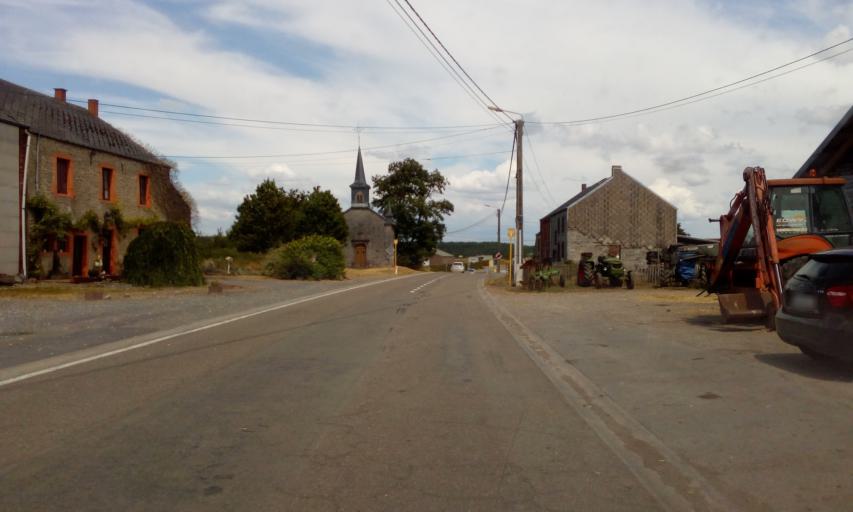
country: BE
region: Wallonia
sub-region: Province du Luxembourg
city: Wellin
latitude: 50.1205
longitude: 5.1116
